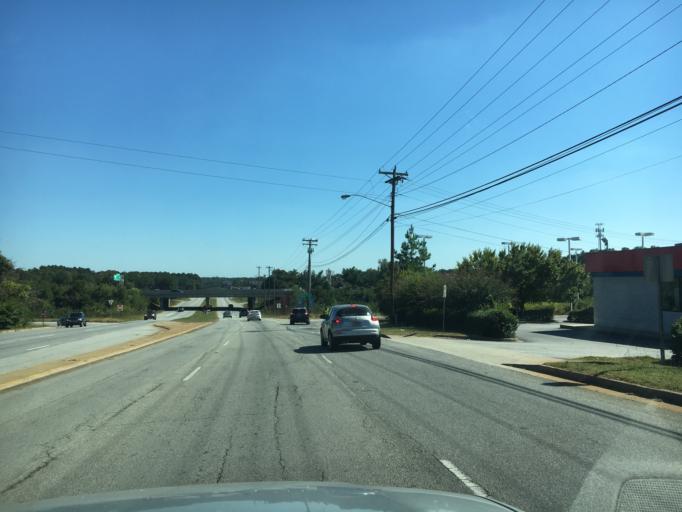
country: US
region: South Carolina
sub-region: Greenville County
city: Mauldin
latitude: 34.8154
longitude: -82.3385
